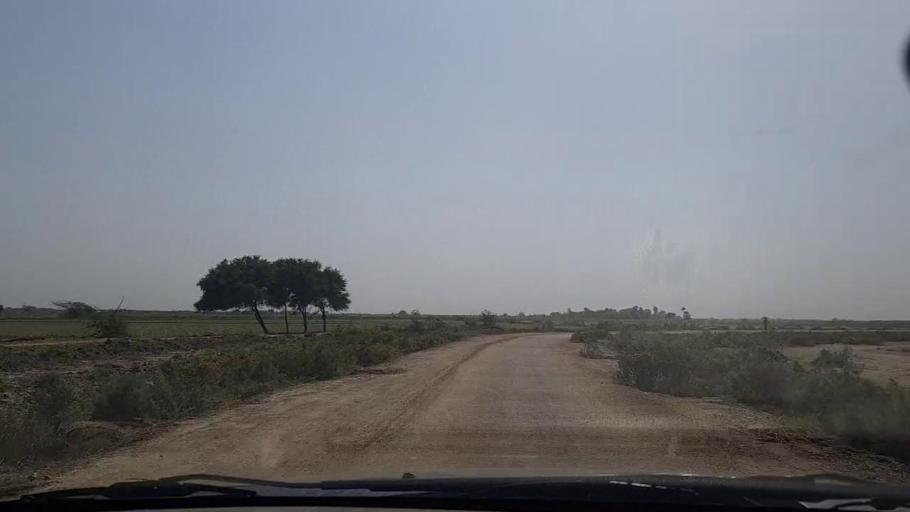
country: PK
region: Sindh
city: Keti Bandar
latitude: 24.2653
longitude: 67.6678
